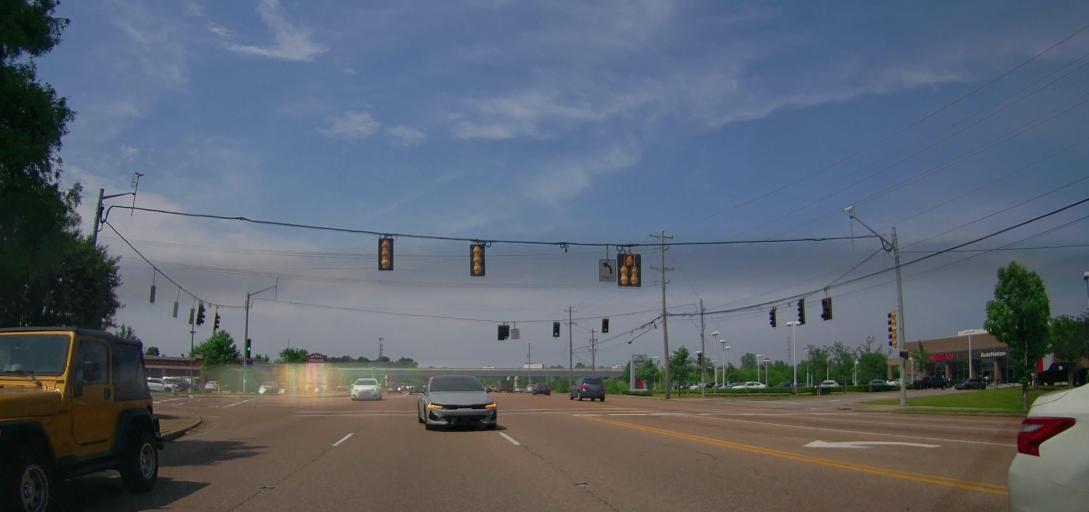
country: US
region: Tennessee
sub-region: Shelby County
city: Germantown
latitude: 35.0348
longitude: -89.7959
